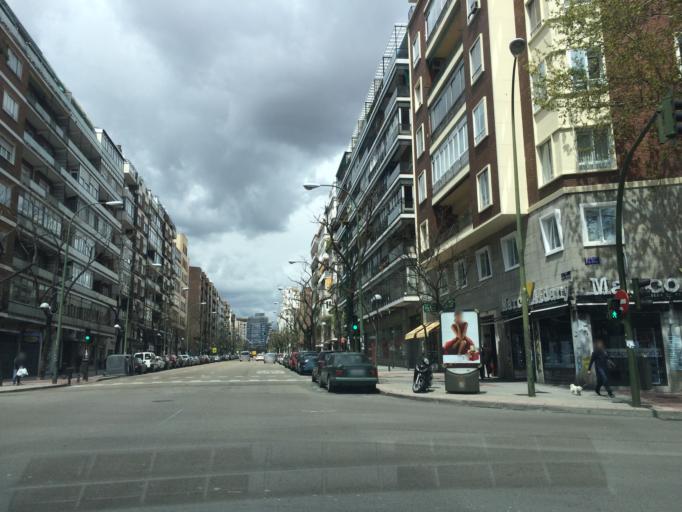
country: ES
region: Madrid
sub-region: Provincia de Madrid
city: Chamberi
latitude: 40.4419
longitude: -3.7017
